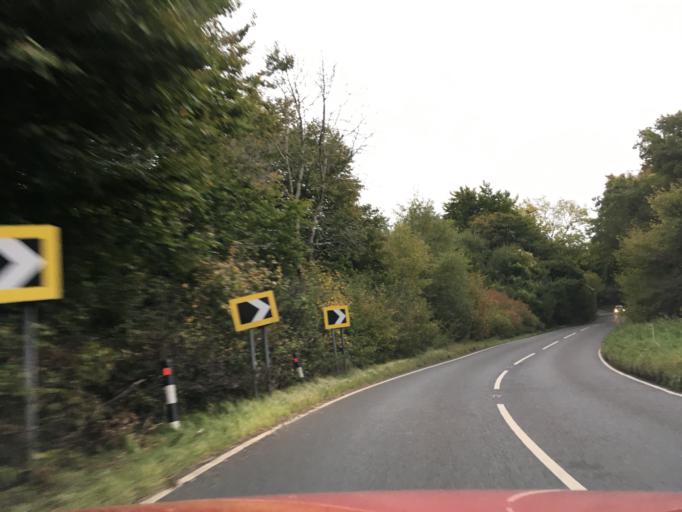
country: GB
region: England
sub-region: Gloucestershire
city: Stonehouse
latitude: 51.7147
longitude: -2.2906
